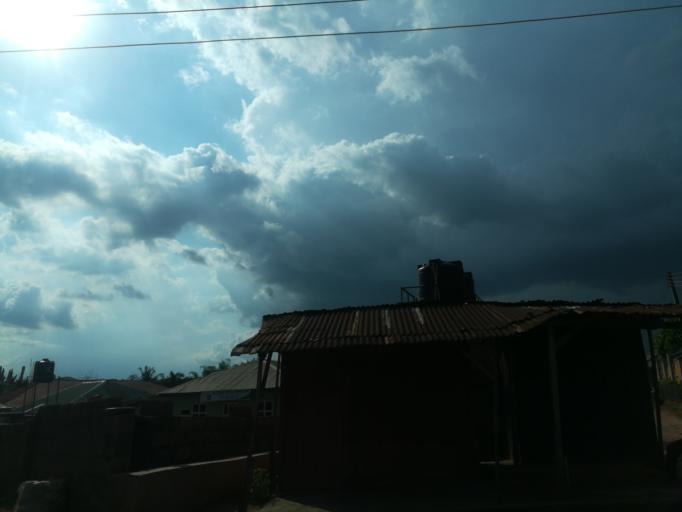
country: NG
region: Oyo
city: Ibadan
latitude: 7.4200
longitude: 3.8363
